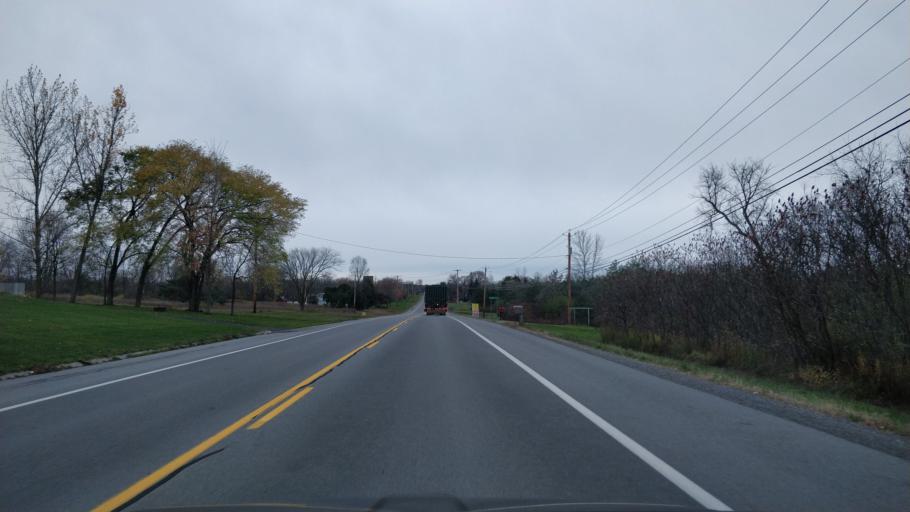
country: CA
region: Ontario
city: Brockville
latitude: 44.6273
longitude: -75.5870
